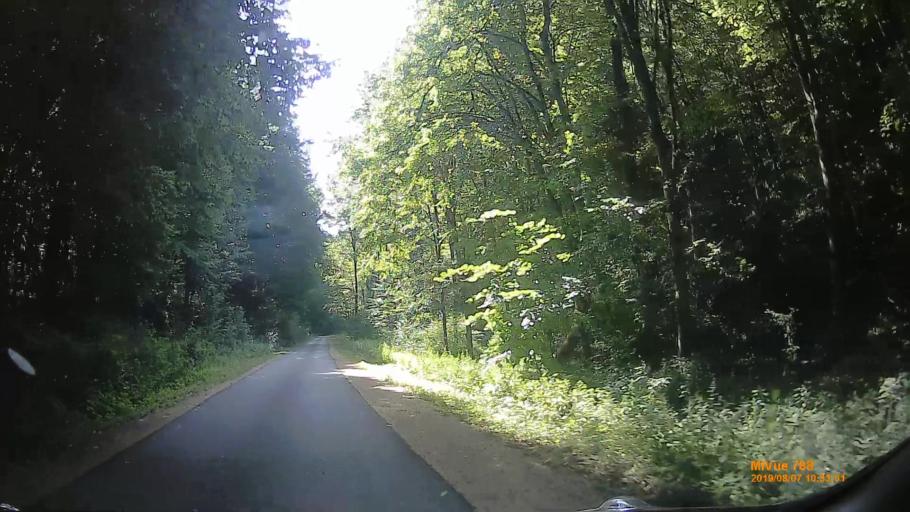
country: HU
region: Veszprem
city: Ajka
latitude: 47.0660
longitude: 17.5907
